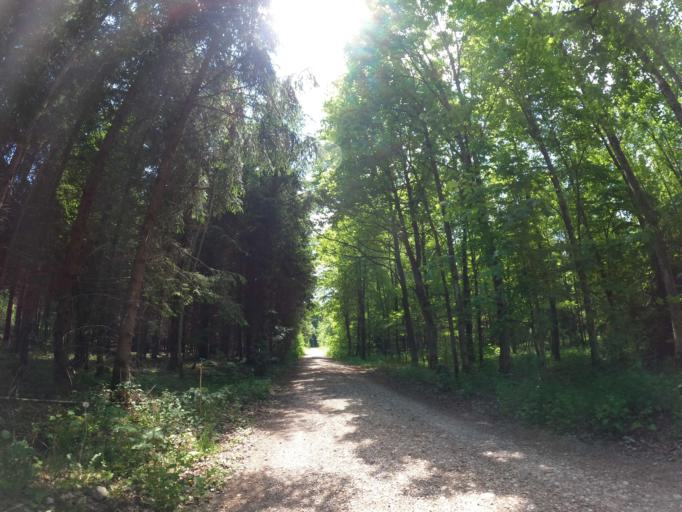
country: DE
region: Bavaria
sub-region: Upper Bavaria
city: Oberhaching
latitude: 48.0184
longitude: 11.6248
